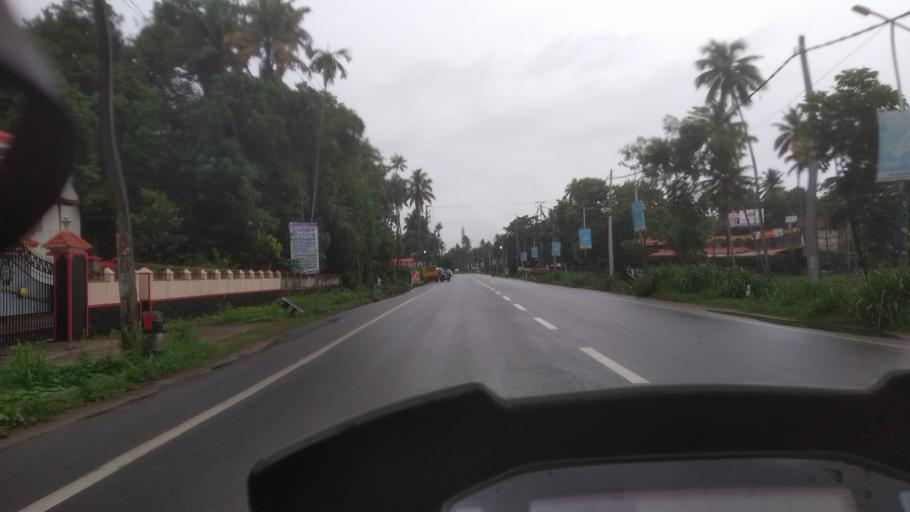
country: IN
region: Kerala
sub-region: Alappuzha
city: Kayankulam
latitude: 9.1325
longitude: 76.5143
